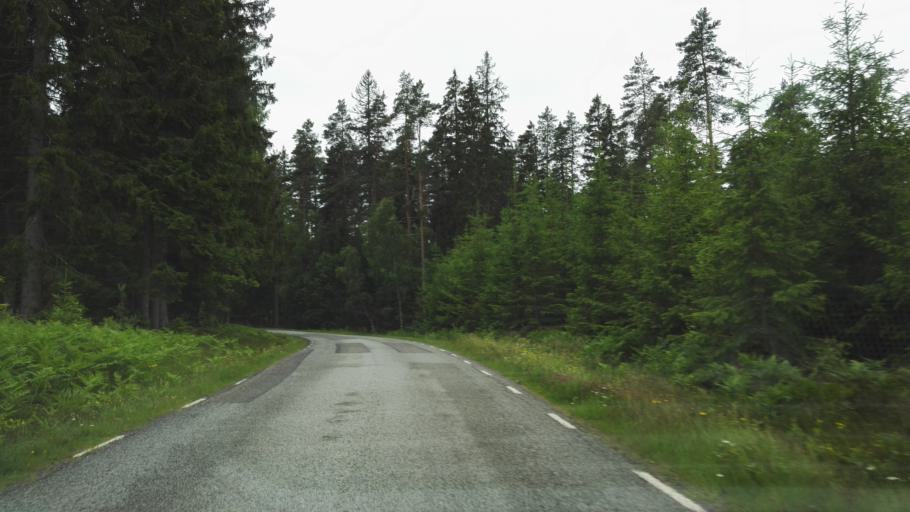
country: SE
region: Kronoberg
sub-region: Vaxjo Kommun
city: Rottne
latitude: 57.1197
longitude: 14.8093
